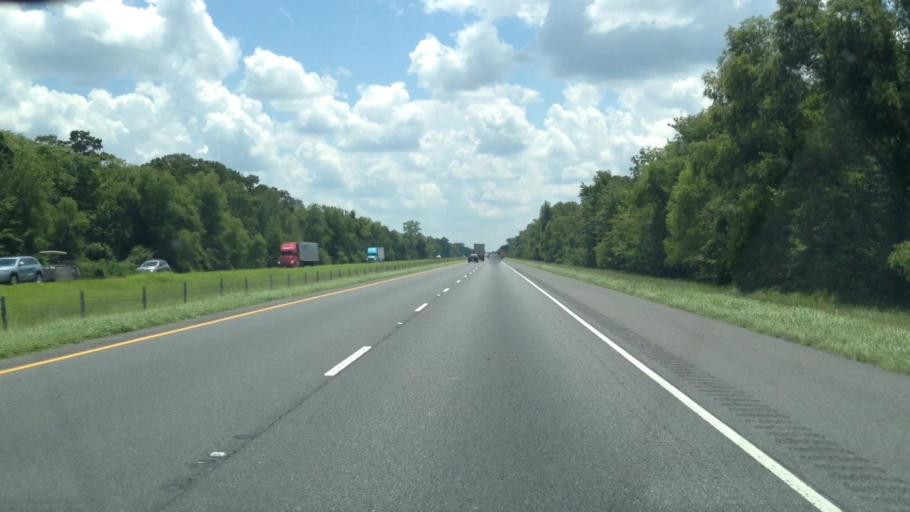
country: US
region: Louisiana
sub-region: Saint James Parish
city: Grand Point
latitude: 30.1417
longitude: -90.7533
